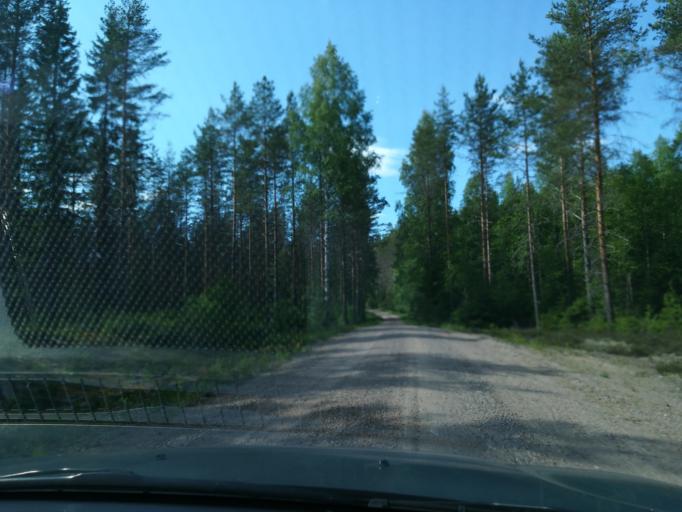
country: FI
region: South Karelia
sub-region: Imatra
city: Ruokolahti
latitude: 61.5369
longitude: 28.8313
